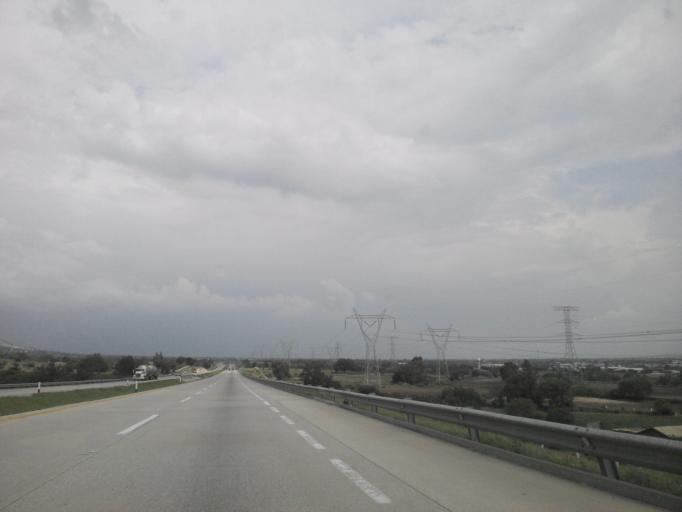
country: MX
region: Mexico
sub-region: Apaxco
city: Colonia Juarez
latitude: 20.0078
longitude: -99.1471
